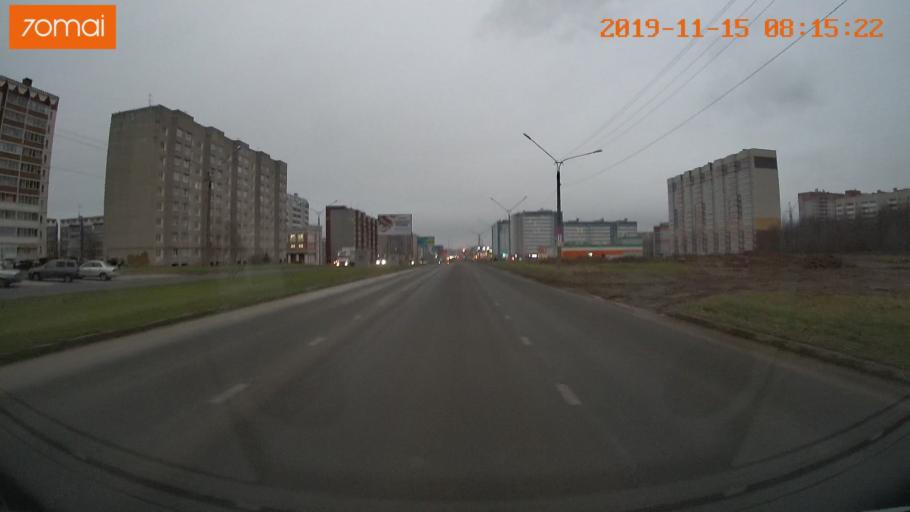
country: RU
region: Vologda
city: Cherepovets
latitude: 59.0817
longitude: 37.9227
